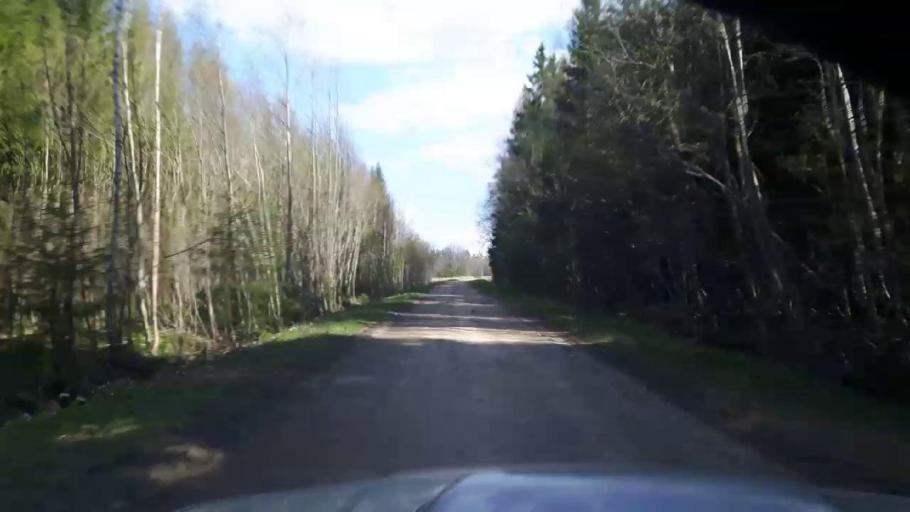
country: EE
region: Paernumaa
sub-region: Tootsi vald
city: Tootsi
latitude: 58.4436
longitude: 24.8754
